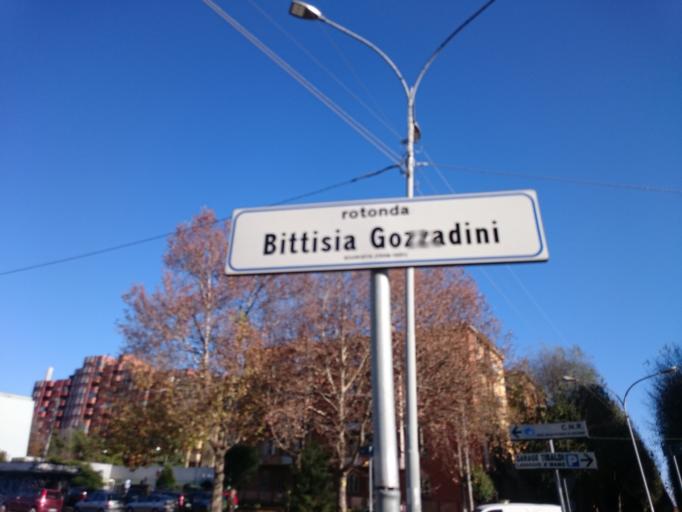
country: IT
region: Emilia-Romagna
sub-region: Provincia di Bologna
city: Bologna
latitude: 44.5170
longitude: 11.3361
